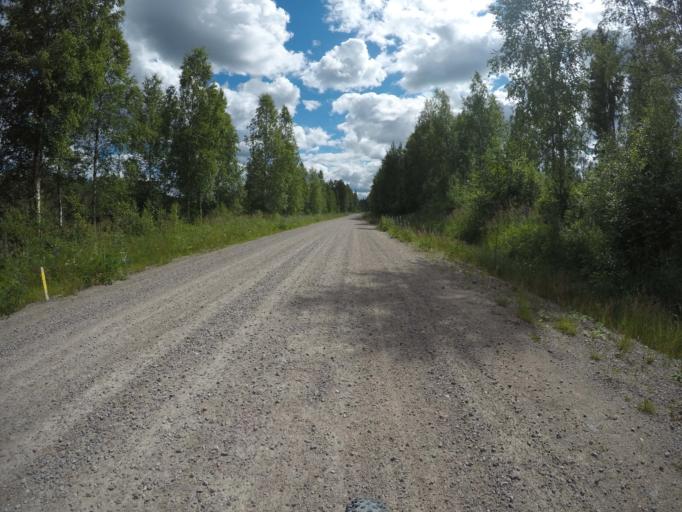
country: SE
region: Vaermland
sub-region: Filipstads Kommun
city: Lesjofors
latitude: 60.1263
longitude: 14.4291
